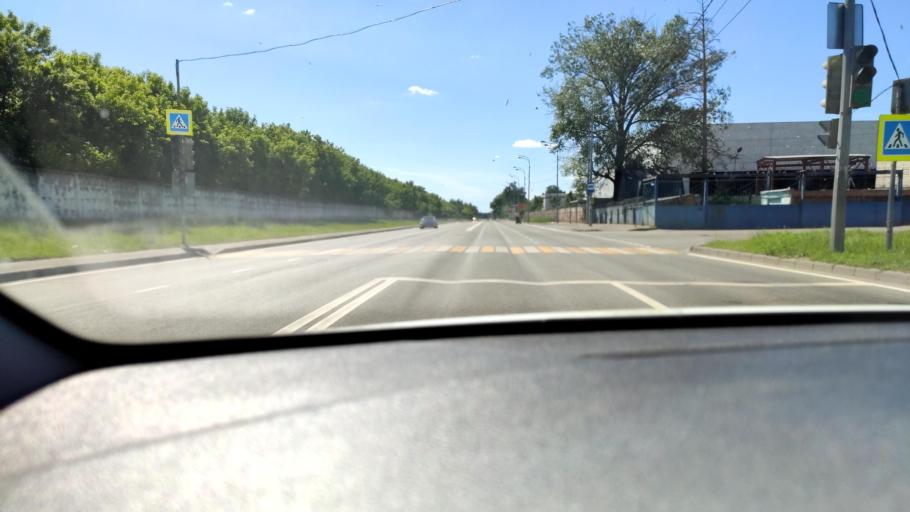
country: RU
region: Tatarstan
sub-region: Gorod Kazan'
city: Kazan
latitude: 55.8397
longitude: 49.0523
